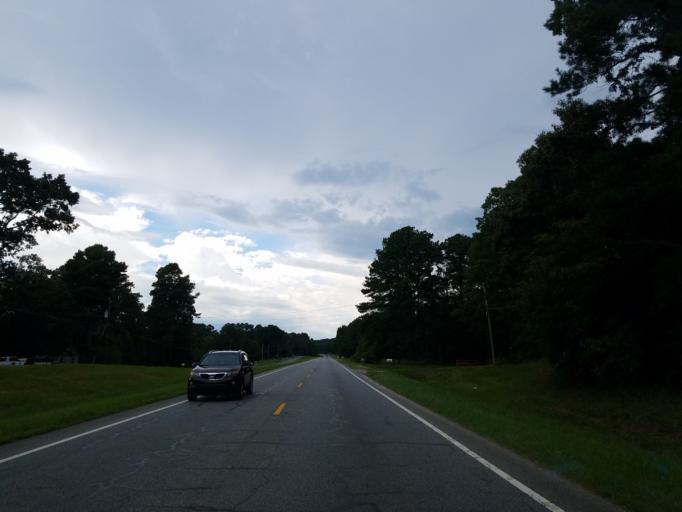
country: US
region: Georgia
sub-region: Bartow County
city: Adairsville
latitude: 34.3038
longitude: -84.8840
